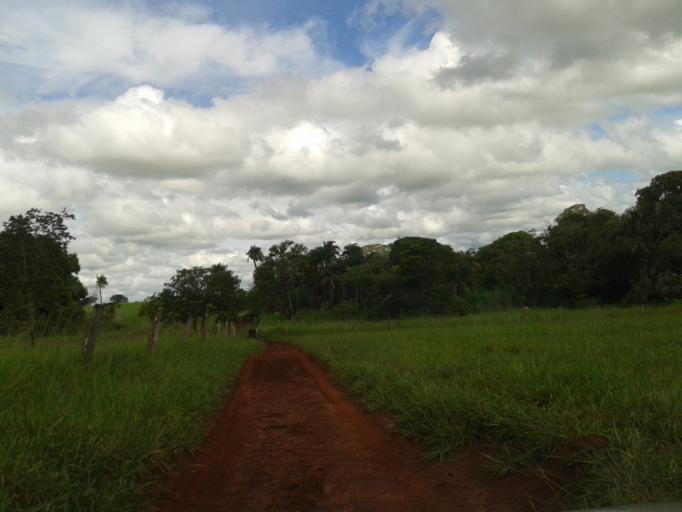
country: BR
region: Minas Gerais
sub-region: Capinopolis
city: Capinopolis
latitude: -18.7772
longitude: -49.7740
